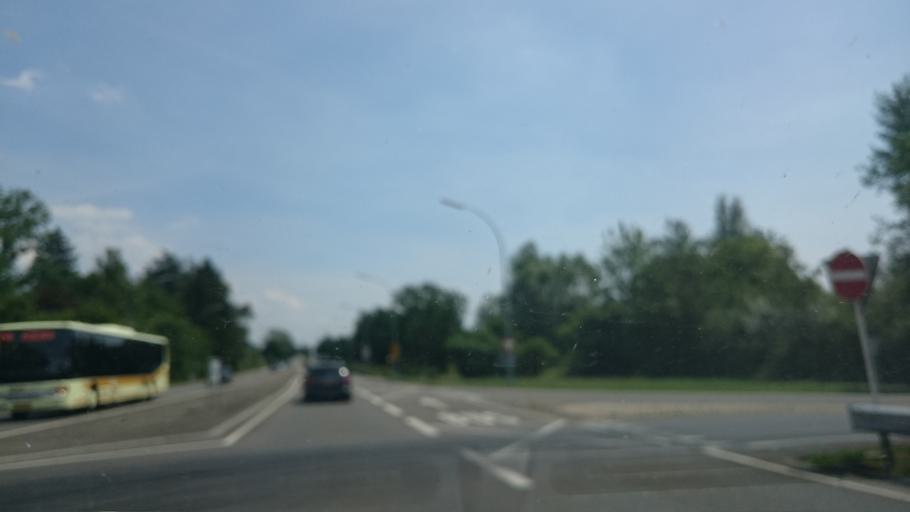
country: LU
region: Luxembourg
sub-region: Canton de Capellen
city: Mamer
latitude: 49.6383
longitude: 6.0086
